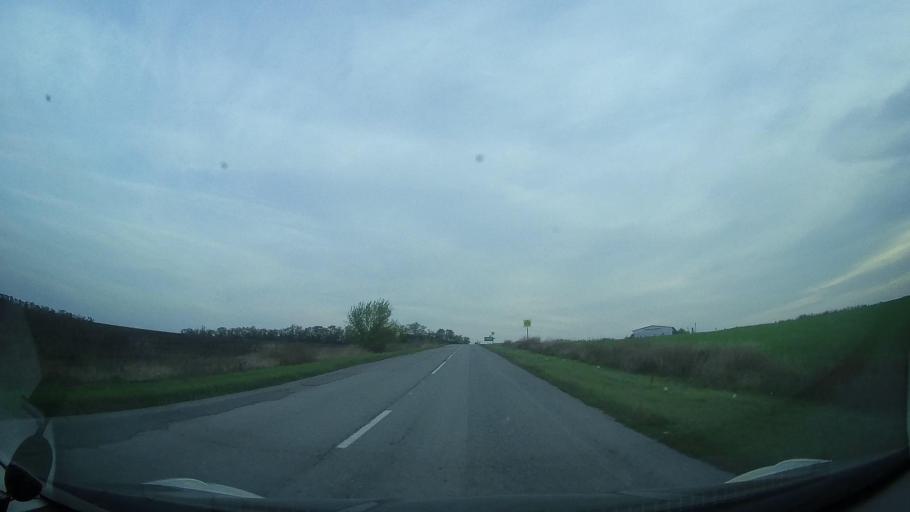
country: RU
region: Rostov
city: Ol'ginskaya
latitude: 47.1246
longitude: 39.9657
